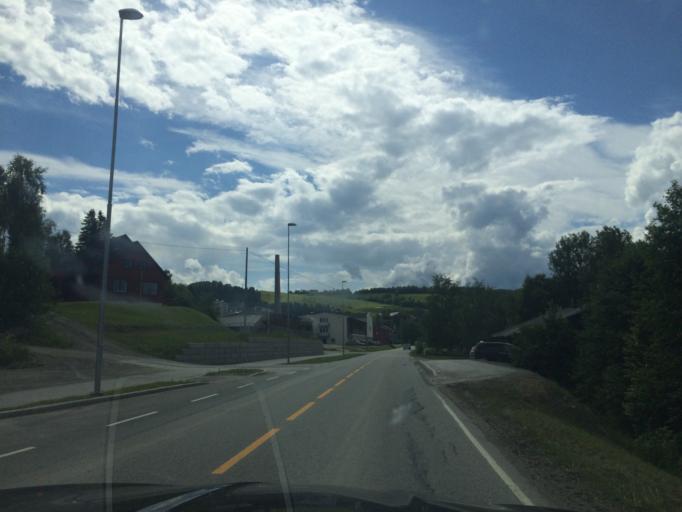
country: NO
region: Sor-Trondelag
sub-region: Selbu
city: Mebonden
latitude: 63.2437
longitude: 11.0886
